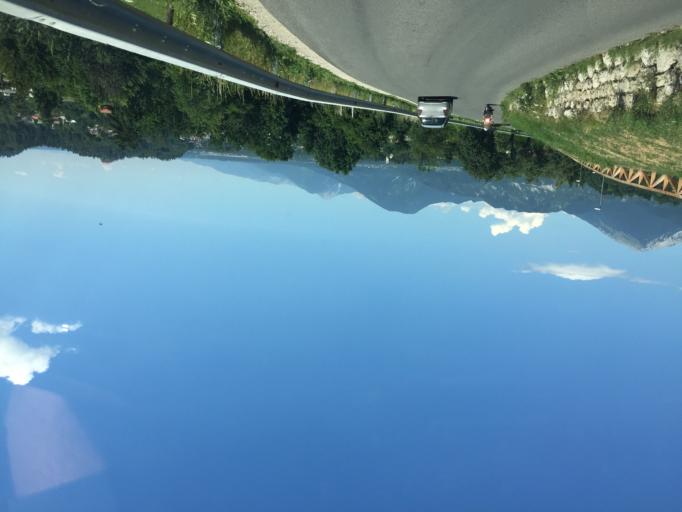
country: SI
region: Gorje
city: Zgornje Gorje
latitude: 46.3796
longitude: 14.0728
